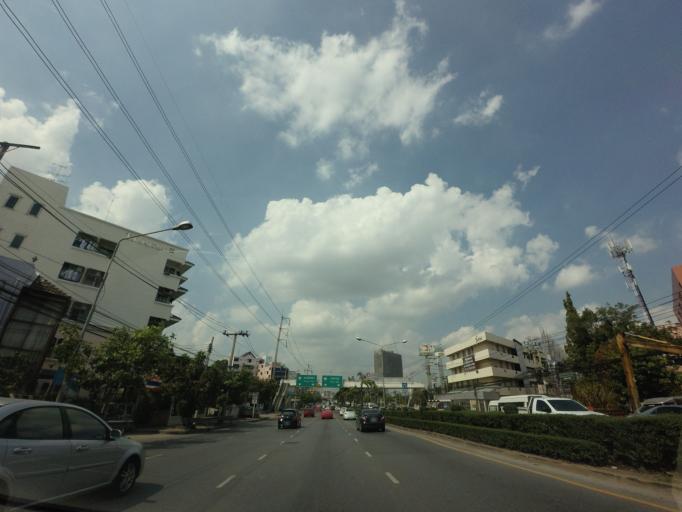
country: TH
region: Bangkok
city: Chatuchak
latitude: 13.8527
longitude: 100.5521
